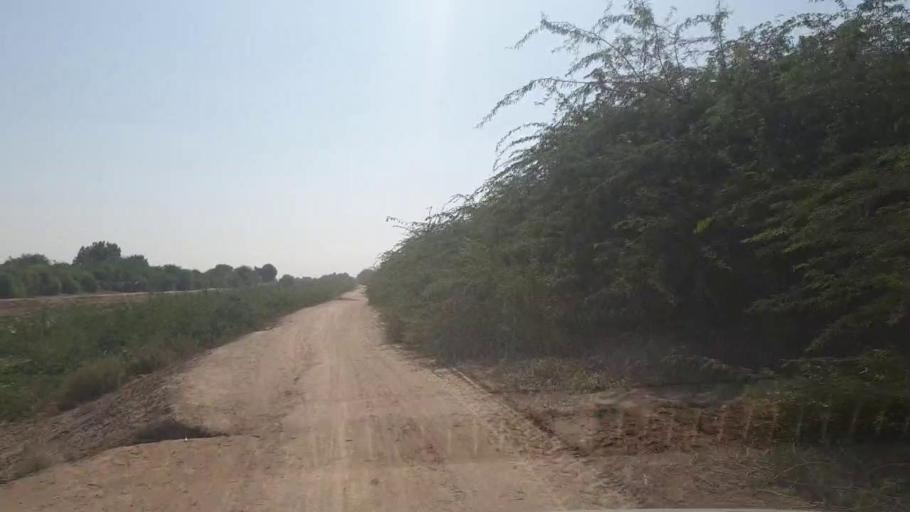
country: PK
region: Sindh
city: Tando Bago
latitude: 24.7695
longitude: 69.1547
